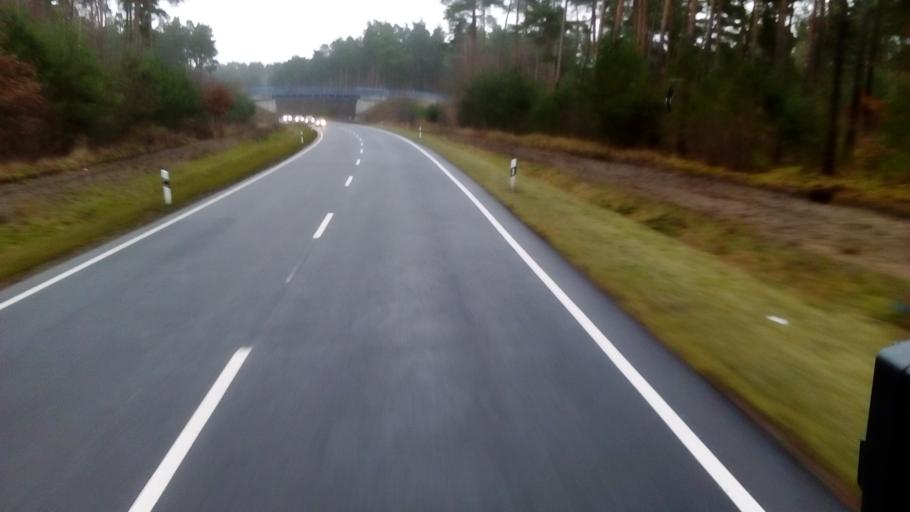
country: DE
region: Brandenburg
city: Perleberg
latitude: 53.0549
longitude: 11.8302
